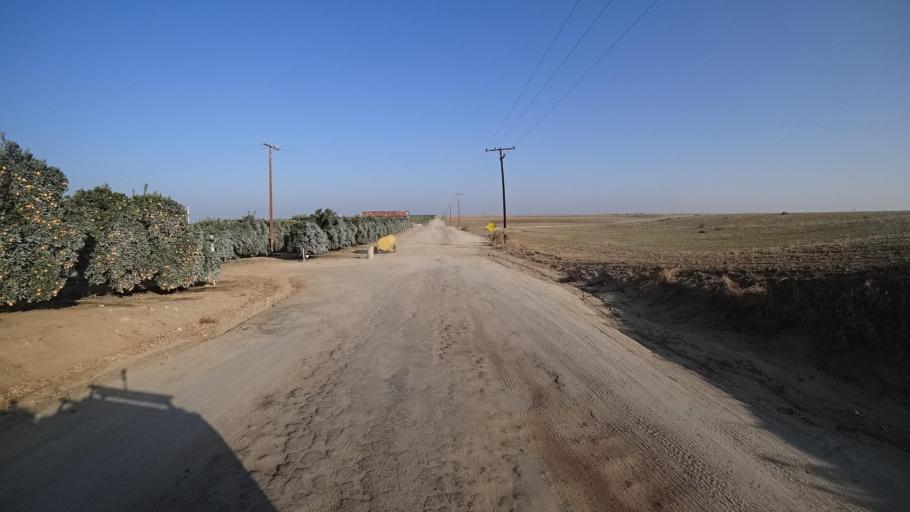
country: US
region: California
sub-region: Tulare County
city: Richgrove
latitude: 35.7687
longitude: -119.0807
